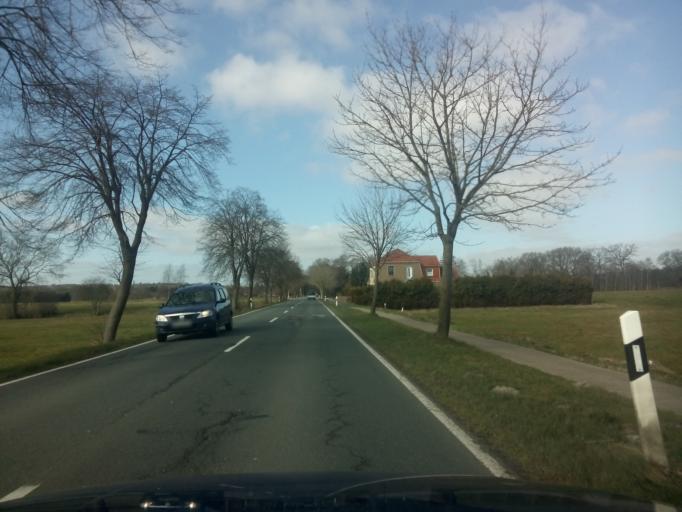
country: DE
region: Lower Saxony
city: Worpswede
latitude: 53.2125
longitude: 8.9591
